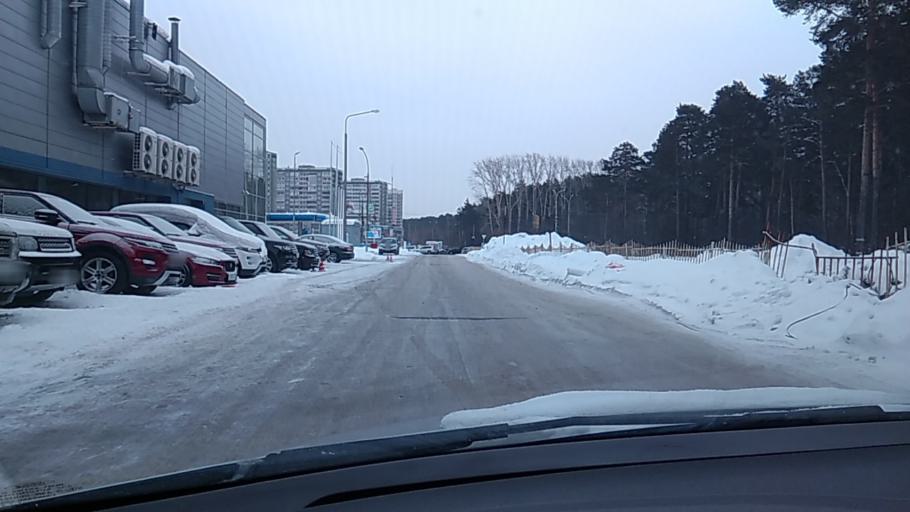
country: RU
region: Sverdlovsk
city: Sovkhoznyy
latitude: 56.7917
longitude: 60.5702
